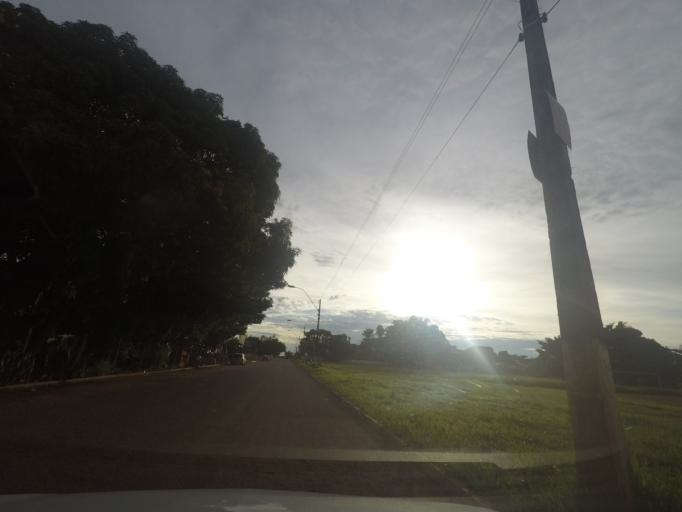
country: BR
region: Goias
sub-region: Trindade
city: Trindade
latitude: -16.7197
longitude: -49.4327
